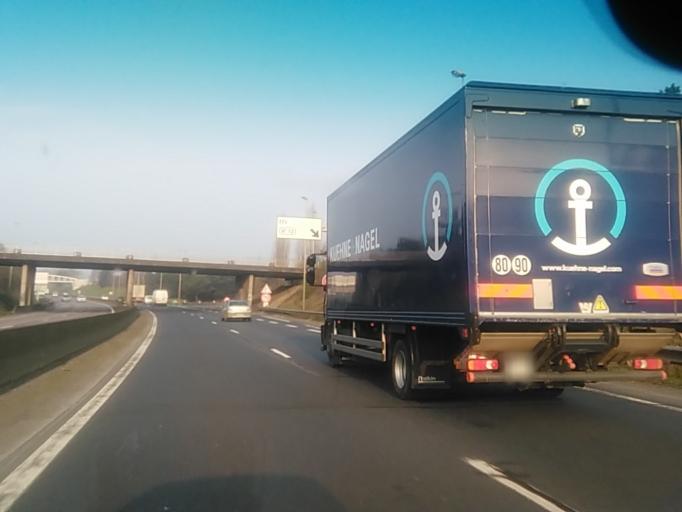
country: FR
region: Lower Normandy
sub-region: Departement du Calvados
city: Ifs
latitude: 49.1474
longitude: -0.3489
